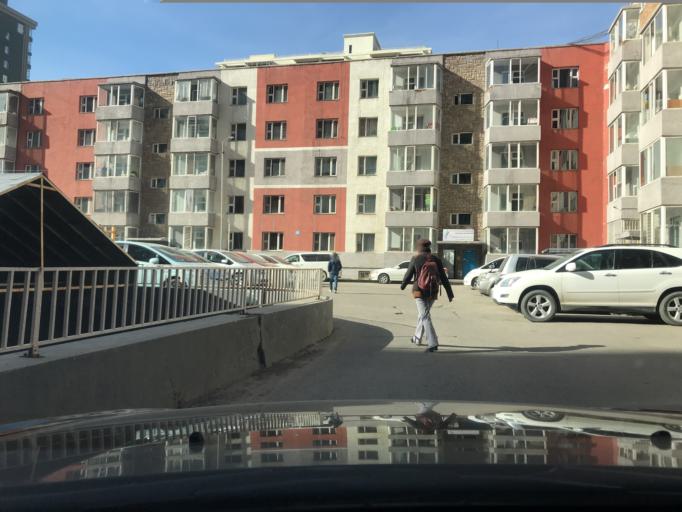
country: MN
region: Ulaanbaatar
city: Ulaanbaatar
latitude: 47.9099
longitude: 106.9411
